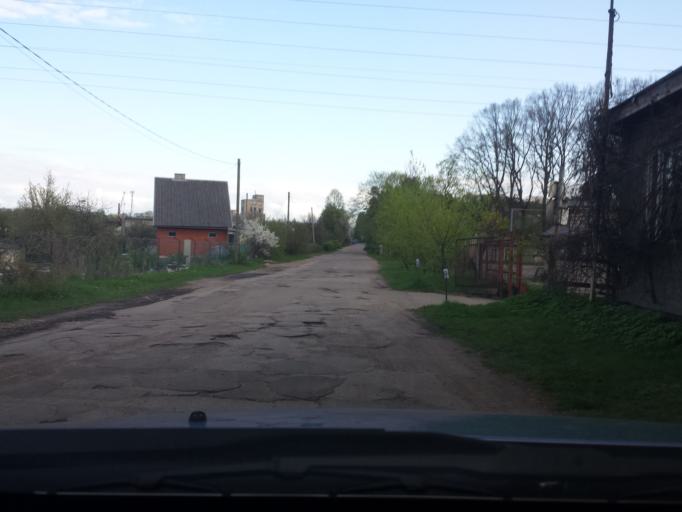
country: LV
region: Riga
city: Jaunciems
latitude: 56.9978
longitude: 24.2240
